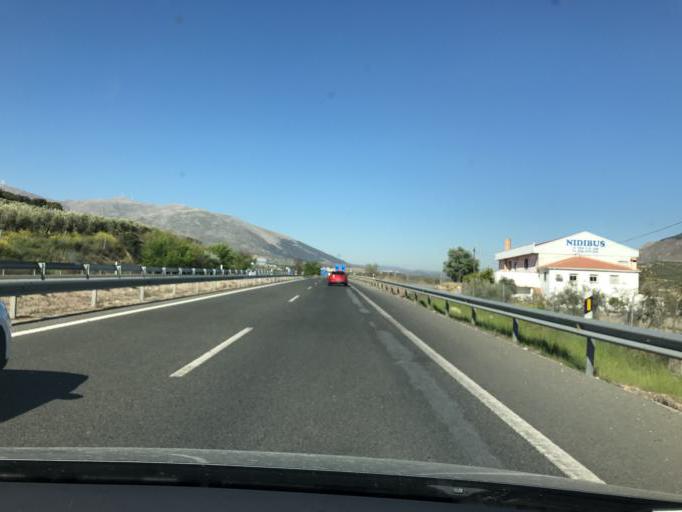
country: ES
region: Andalusia
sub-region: Provincia de Granada
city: Salar
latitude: 37.1662
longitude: -4.0937
